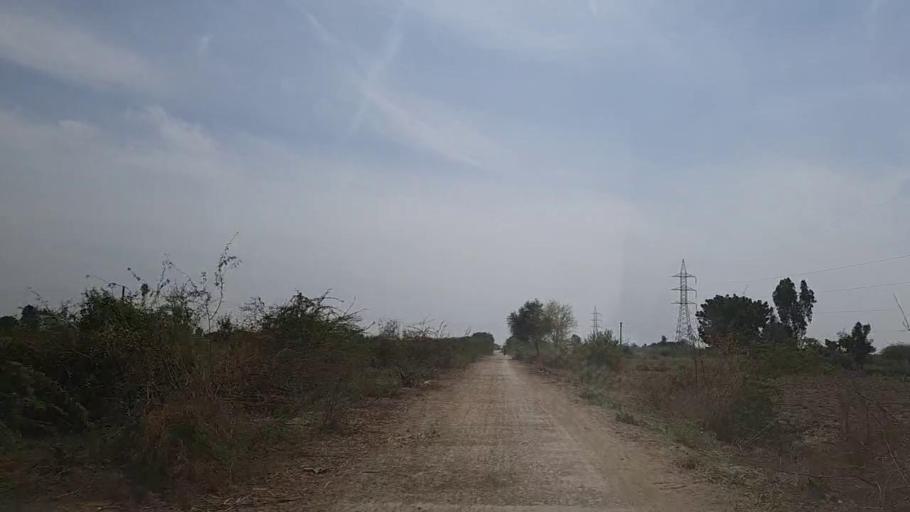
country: PK
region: Sindh
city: Kunri
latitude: 25.1934
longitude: 69.4617
